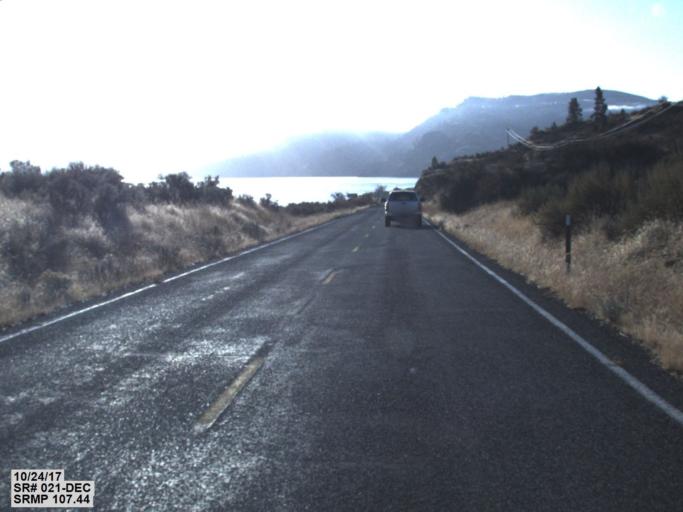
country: US
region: Washington
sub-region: Okanogan County
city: Coulee Dam
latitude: 47.9569
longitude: -118.6956
